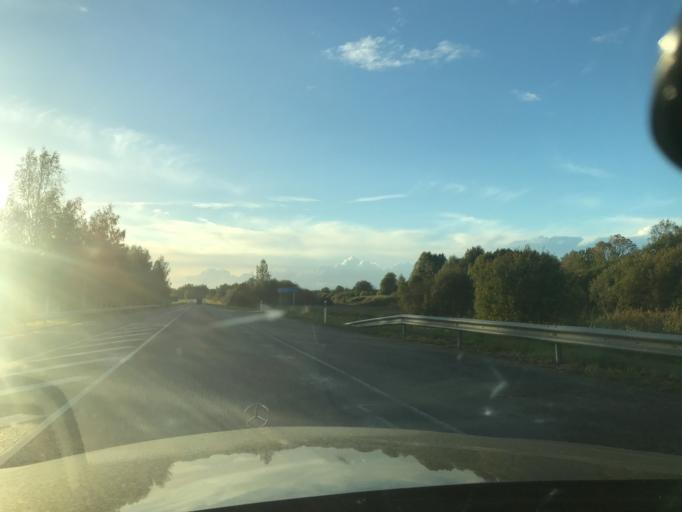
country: EE
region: Vorumaa
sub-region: Voru linn
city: Voru
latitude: 57.8602
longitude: 26.9974
